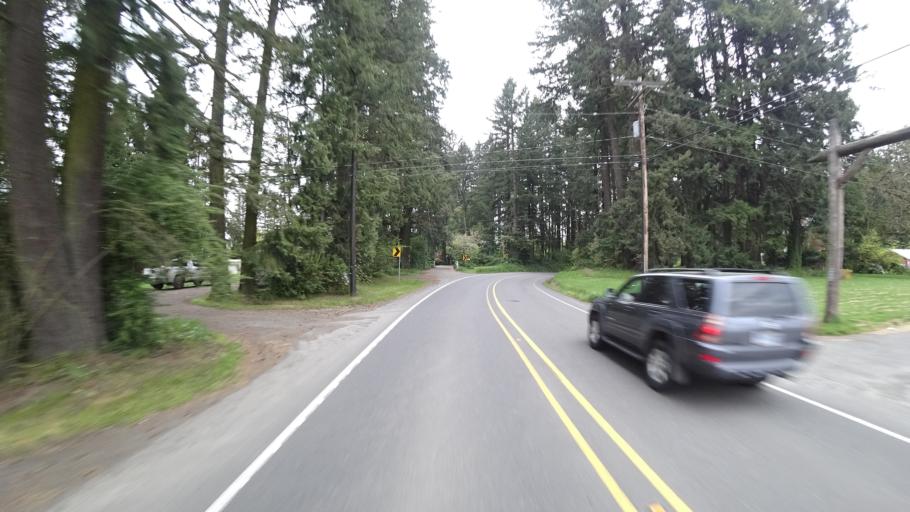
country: US
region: Oregon
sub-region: Washington County
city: North Plains
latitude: 45.5635
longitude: -122.9727
